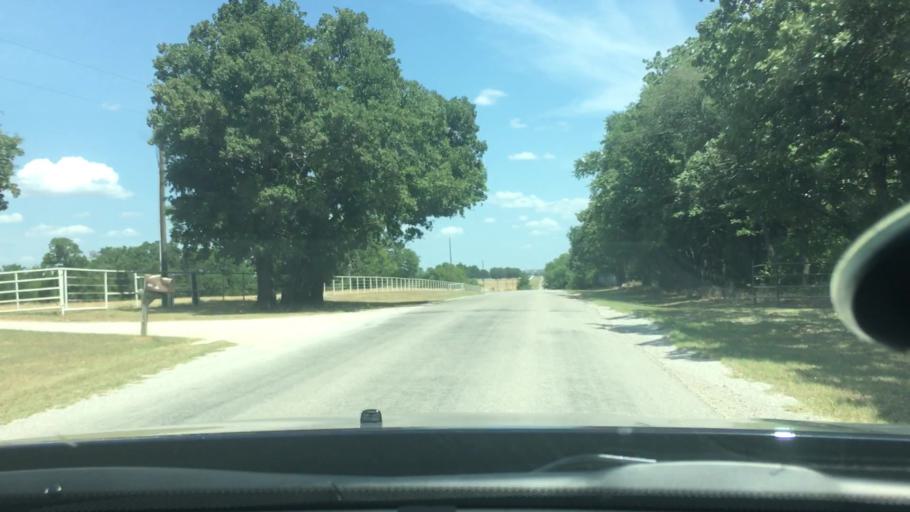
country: US
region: Oklahoma
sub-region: Love County
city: Marietta
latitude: 34.0371
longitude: -97.1957
